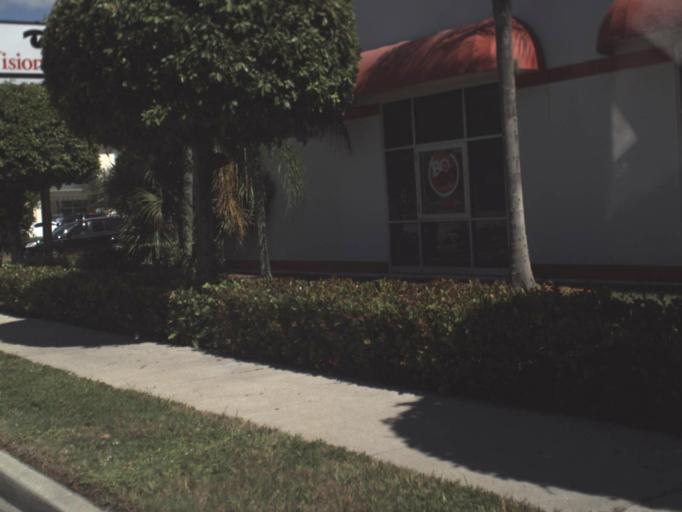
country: US
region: Florida
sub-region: Collier County
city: Naples
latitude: 26.1739
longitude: -81.7995
